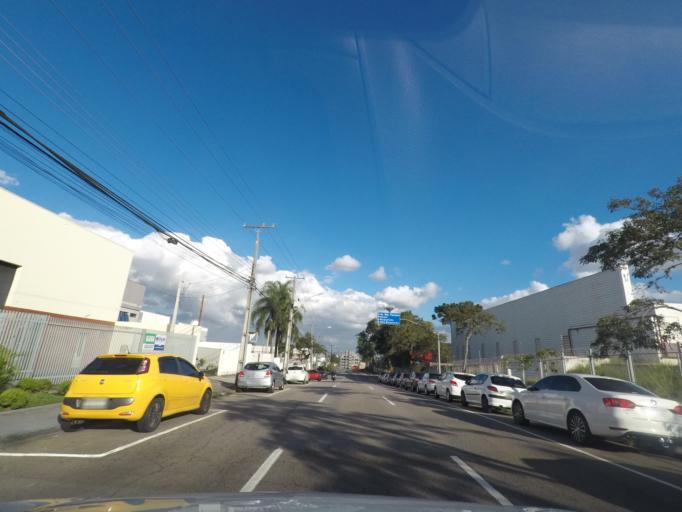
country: BR
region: Parana
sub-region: Curitiba
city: Curitiba
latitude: -25.4642
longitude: -49.2580
